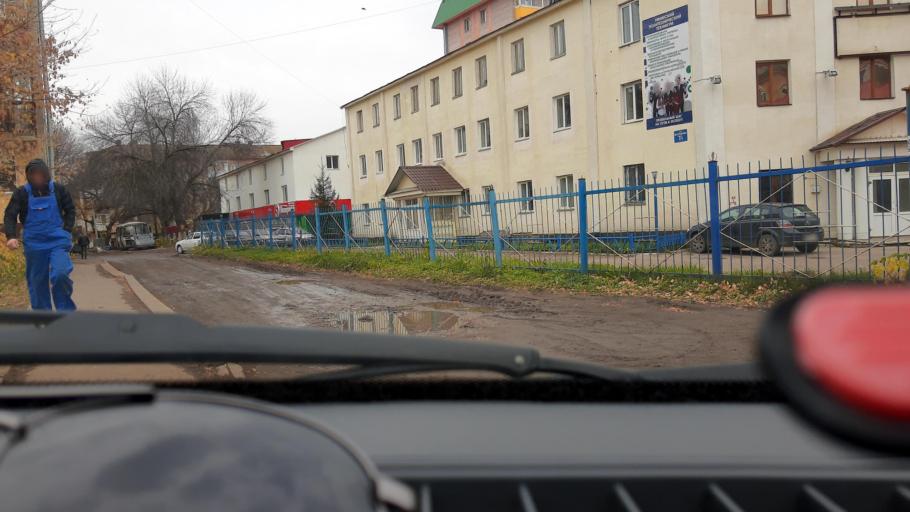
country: RU
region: Bashkortostan
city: Ufa
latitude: 54.8027
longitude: 56.1233
